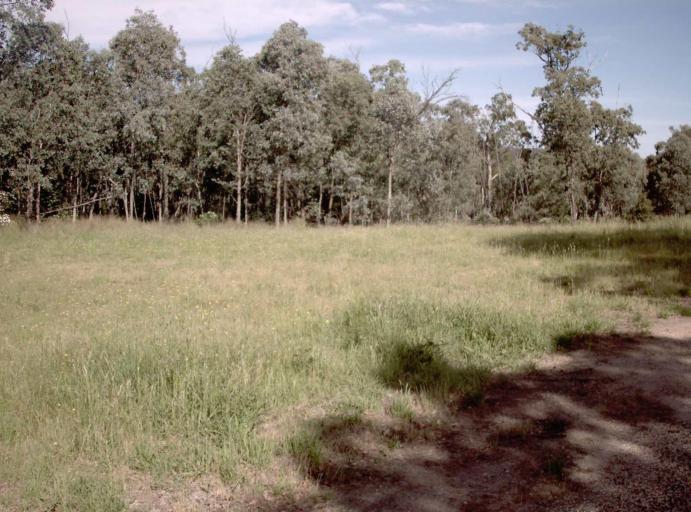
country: AU
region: Victoria
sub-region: East Gippsland
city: Lakes Entrance
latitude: -37.4842
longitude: 148.1277
